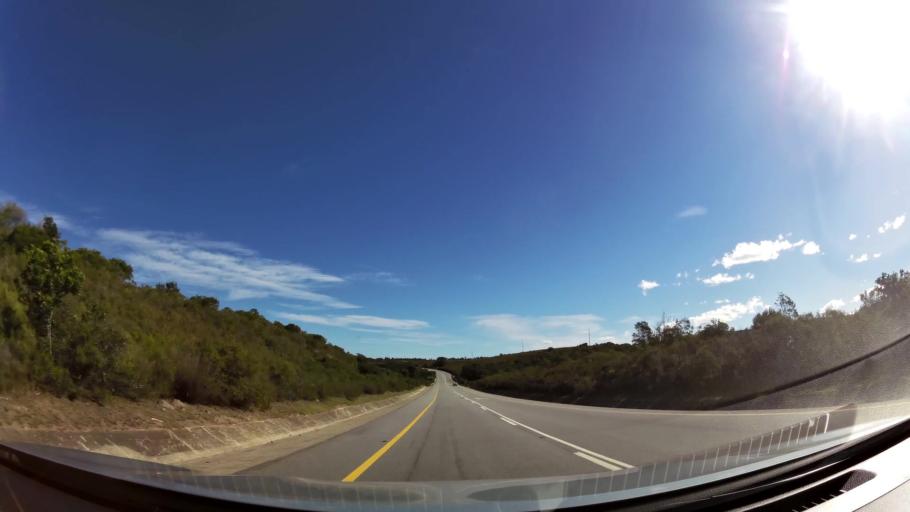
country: ZA
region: Eastern Cape
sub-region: Cacadu District Municipality
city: Kruisfontein
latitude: -34.0140
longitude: 24.6383
